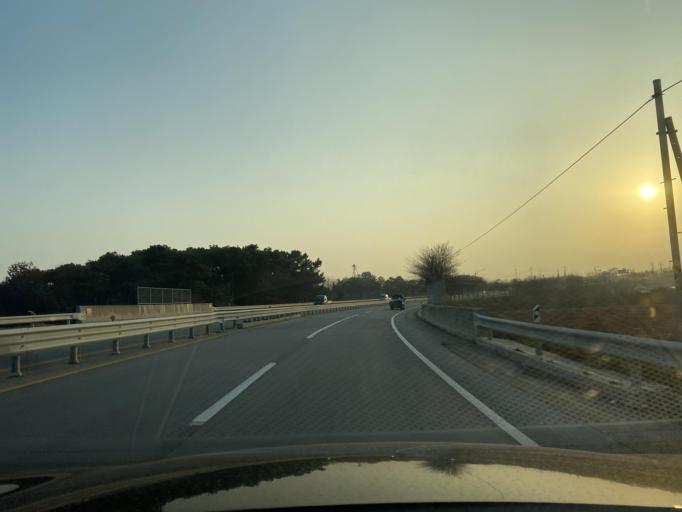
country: KR
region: Chungcheongnam-do
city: Yesan
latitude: 36.6920
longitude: 126.7943
